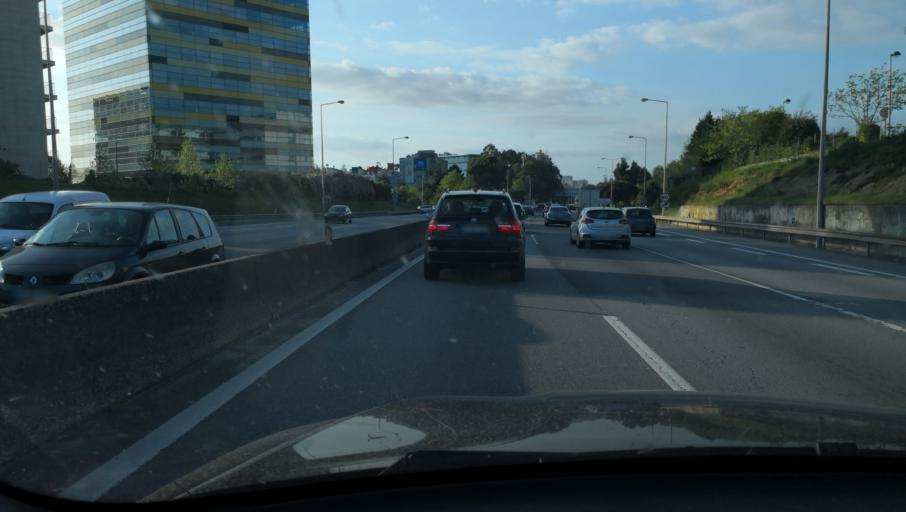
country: PT
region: Porto
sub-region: Vila Nova de Gaia
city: Canidelo
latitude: 41.1414
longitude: -8.6386
